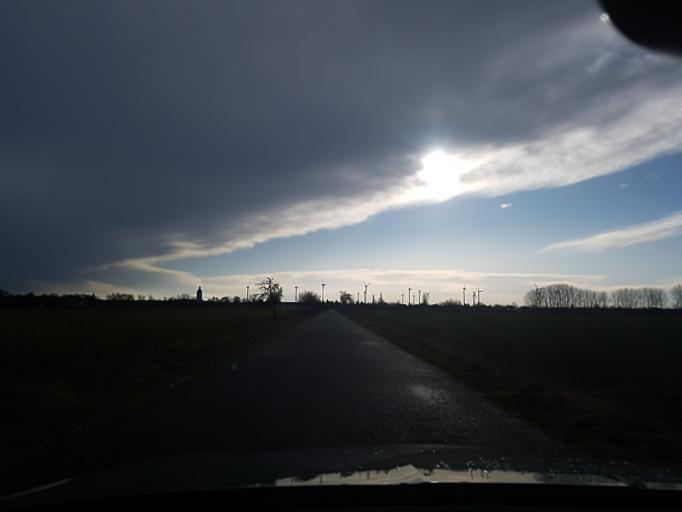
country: DE
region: Brandenburg
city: Falkenberg
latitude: 51.6015
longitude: 13.2914
